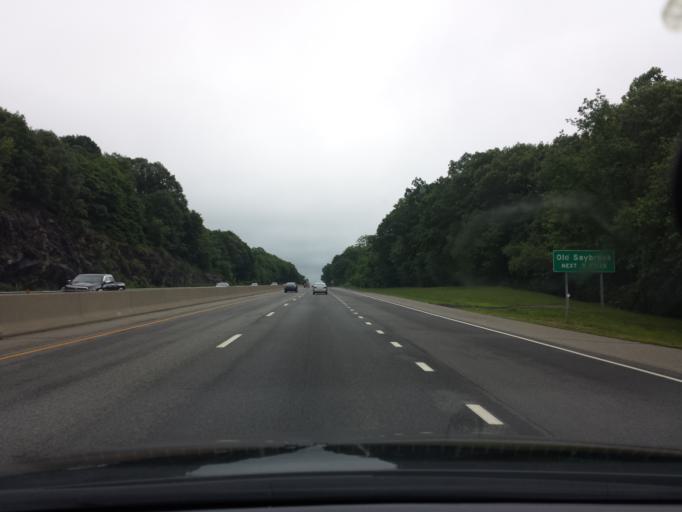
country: US
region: Connecticut
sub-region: Middlesex County
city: Westbrook Center
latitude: 41.2915
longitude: -72.4414
